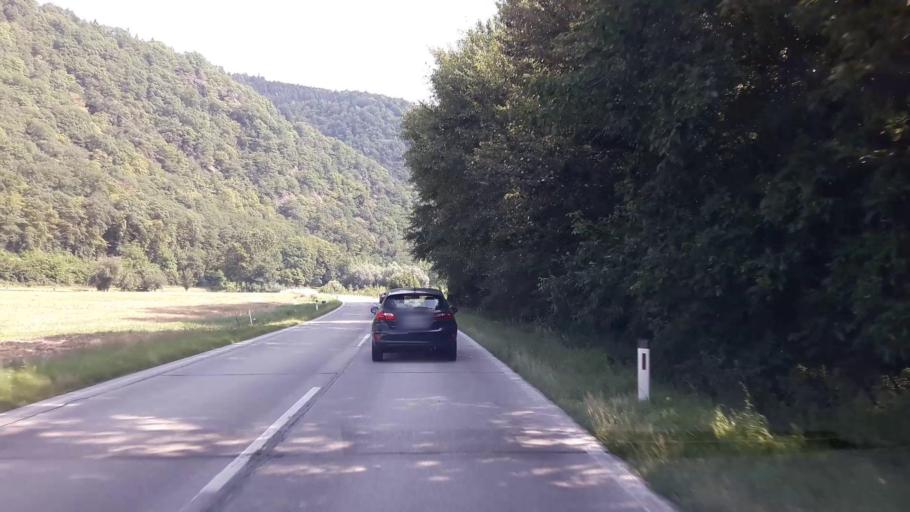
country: AT
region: Lower Austria
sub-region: Politischer Bezirk Krems
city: Aggsbach
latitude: 48.2688
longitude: 15.3748
